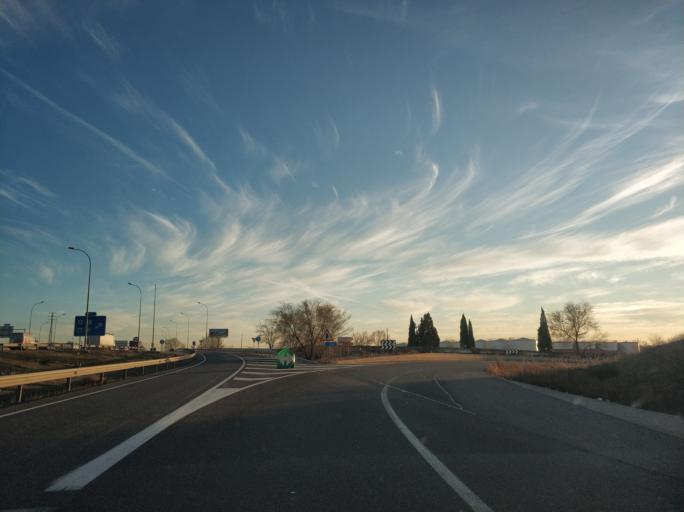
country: ES
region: Madrid
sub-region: Provincia de Madrid
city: Pinto
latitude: 40.2309
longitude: -3.6899
